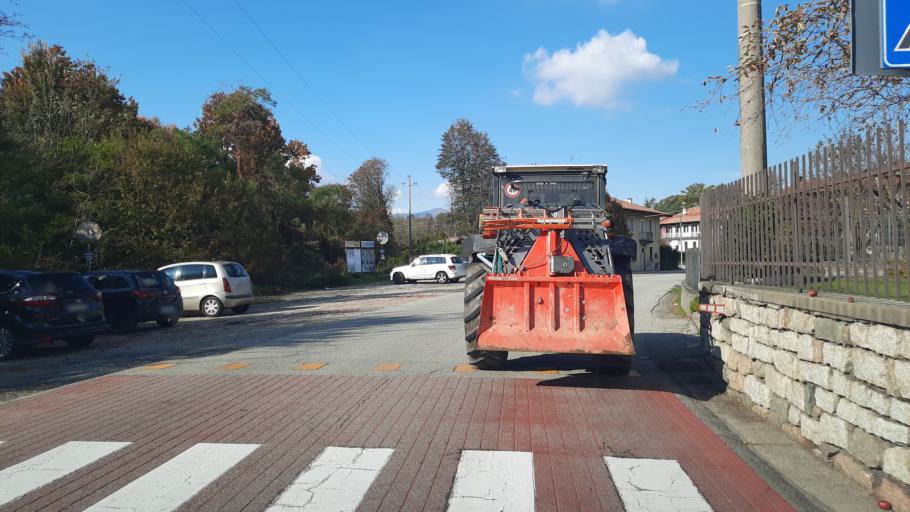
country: IT
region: Piedmont
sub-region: Provincia di Novara
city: Ameno
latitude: 45.7797
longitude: 8.4349
